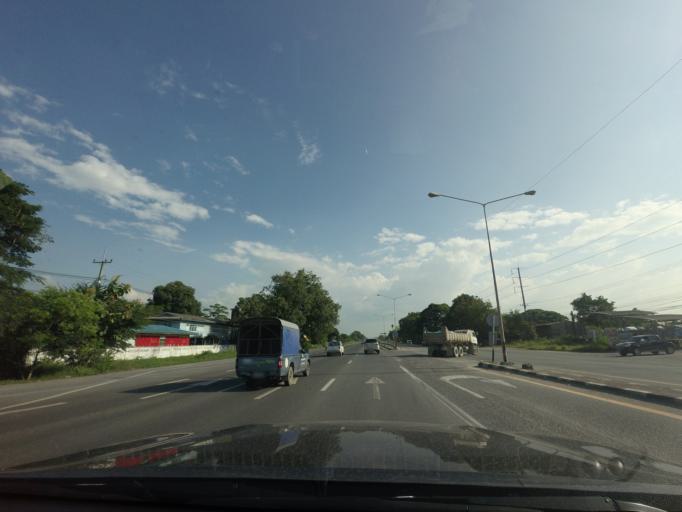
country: TH
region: Sara Buri
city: Chaloem Phra Kiat
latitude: 14.6415
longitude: 100.8866
